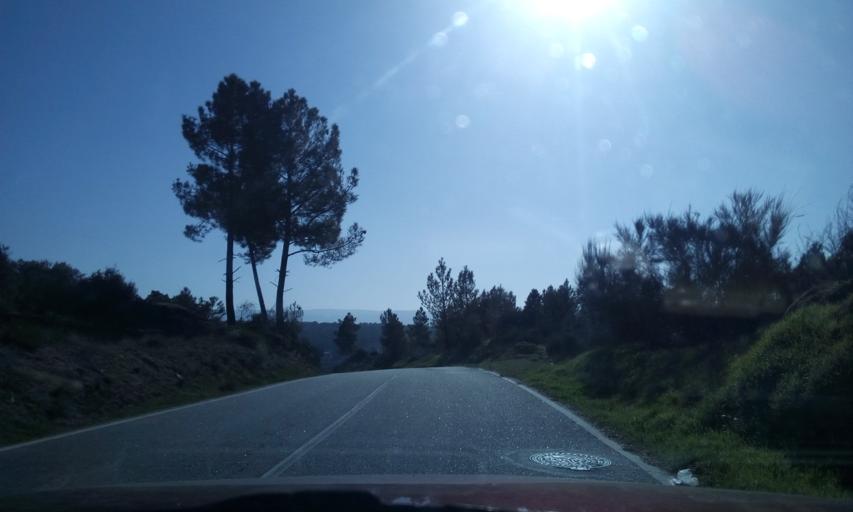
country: PT
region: Guarda
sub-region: Celorico da Beira
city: Celorico da Beira
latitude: 40.6707
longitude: -7.3915
